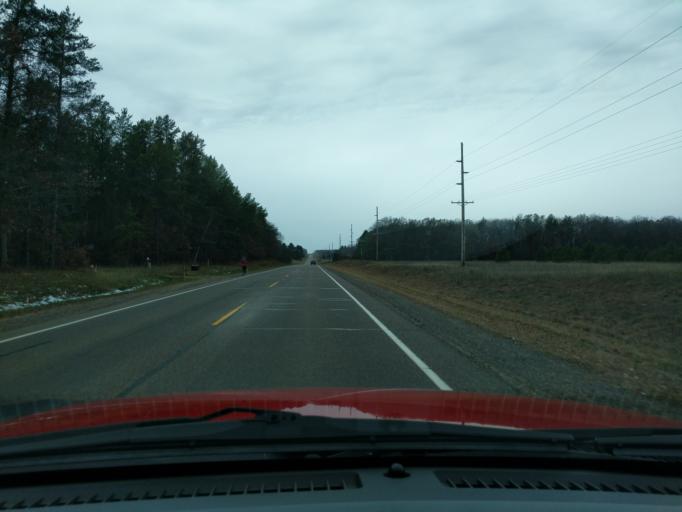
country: US
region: Wisconsin
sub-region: Washburn County
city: Shell Lake
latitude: 45.8151
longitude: -91.9988
